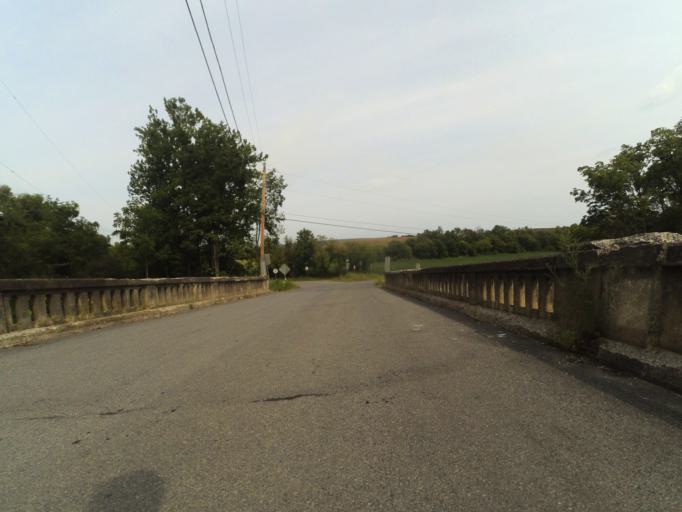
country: US
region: Pennsylvania
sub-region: Huntingdon County
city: Huntingdon
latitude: 40.5826
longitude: -78.0460
